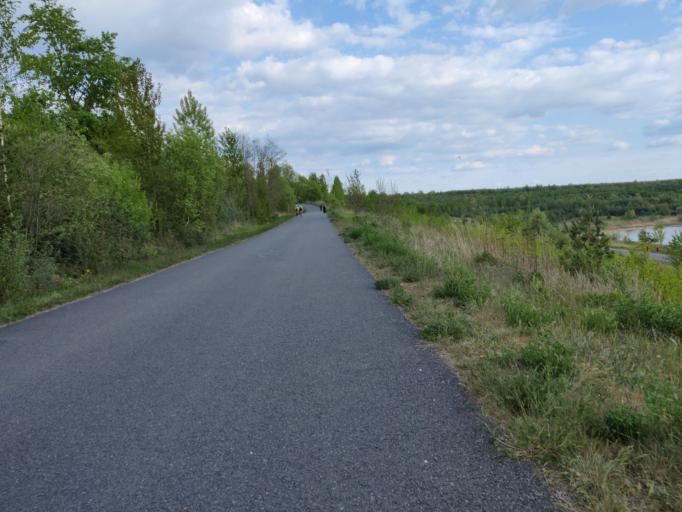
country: DE
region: Saxony
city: Grossposna
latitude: 51.2400
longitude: 12.4782
